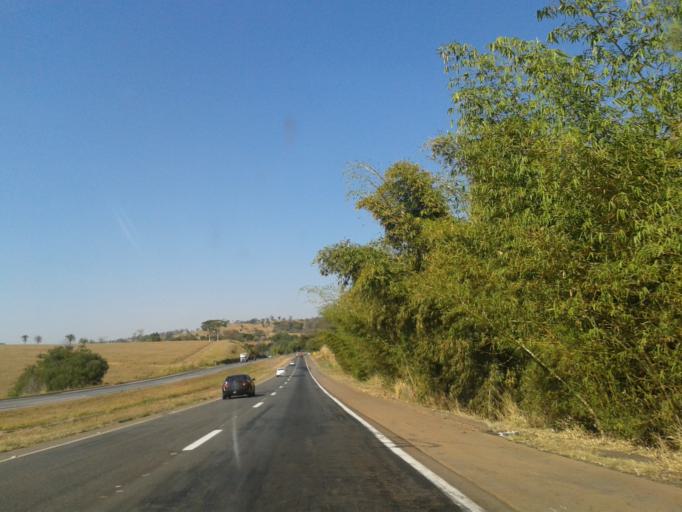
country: BR
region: Goias
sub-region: Piracanjuba
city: Piracanjuba
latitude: -17.1949
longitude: -49.2088
